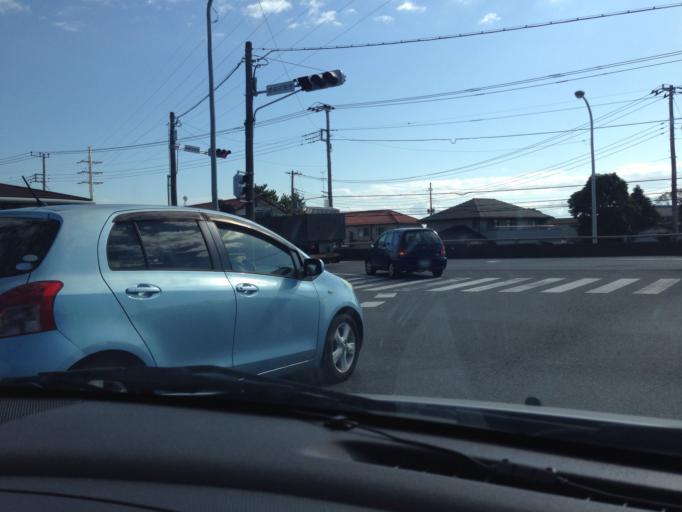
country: JP
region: Ibaraki
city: Ami
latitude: 36.0825
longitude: 140.2100
